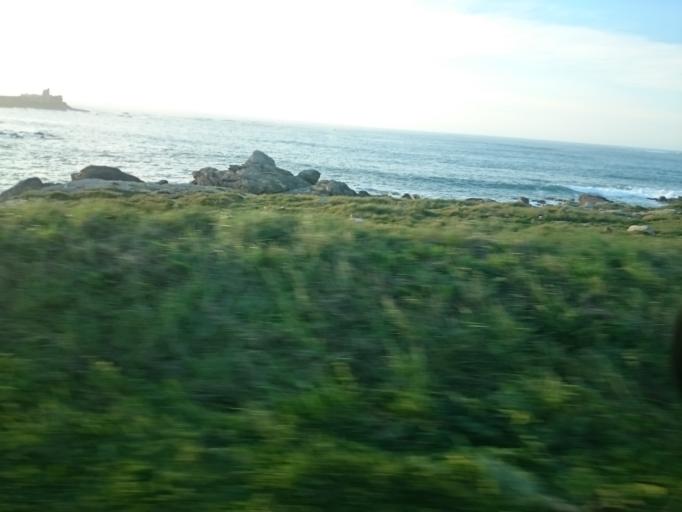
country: FR
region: Brittany
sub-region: Departement du Finistere
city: Landunvez
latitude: 48.5347
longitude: -4.7492
